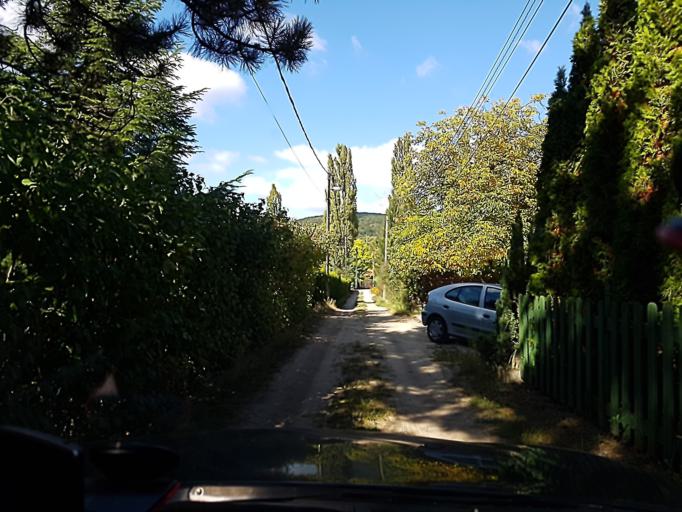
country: HU
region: Pest
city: Piliscsaba
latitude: 47.6371
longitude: 18.8536
